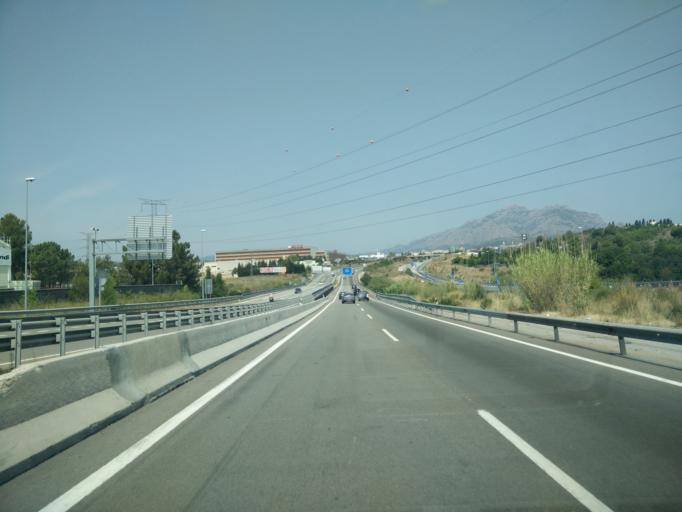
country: ES
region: Catalonia
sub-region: Provincia de Barcelona
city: Abrera
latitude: 41.5233
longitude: 1.8856
